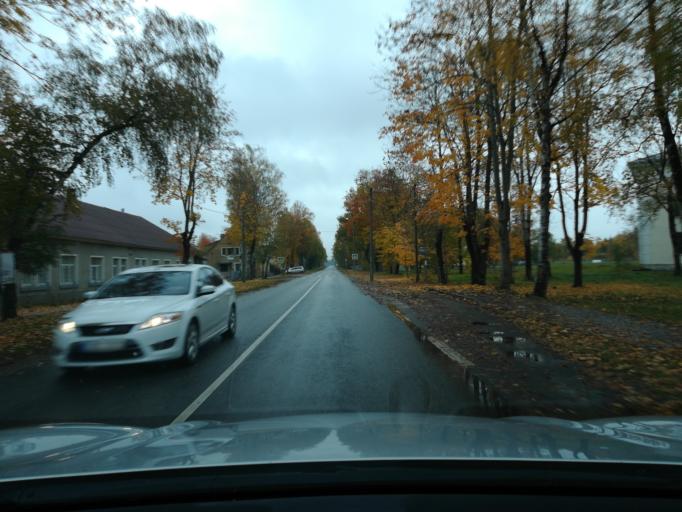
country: EE
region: Ida-Virumaa
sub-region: Johvi vald
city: Johvi
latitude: 59.3121
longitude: 27.4522
